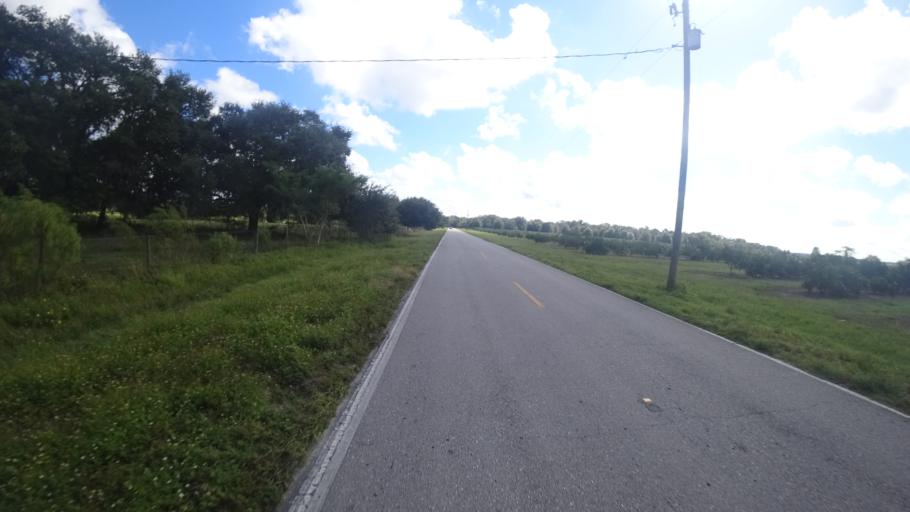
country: US
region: Florida
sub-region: Sarasota County
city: Lake Sarasota
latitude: 27.3453
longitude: -82.2340
